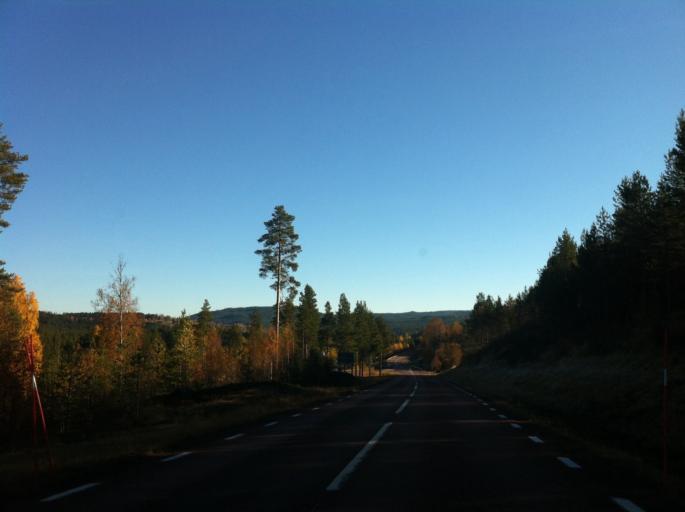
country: SE
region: Dalarna
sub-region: Alvdalens Kommun
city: AElvdalen
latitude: 61.2905
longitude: 13.7414
